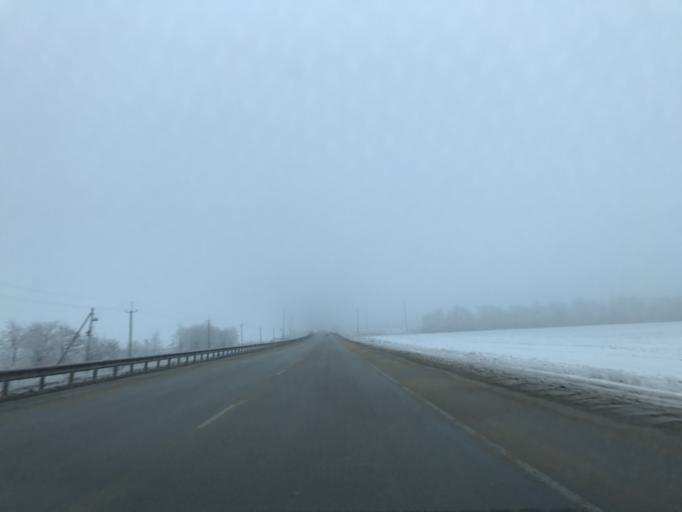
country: RU
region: Rostov
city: Grushevskaya
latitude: 47.3786
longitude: 39.8588
